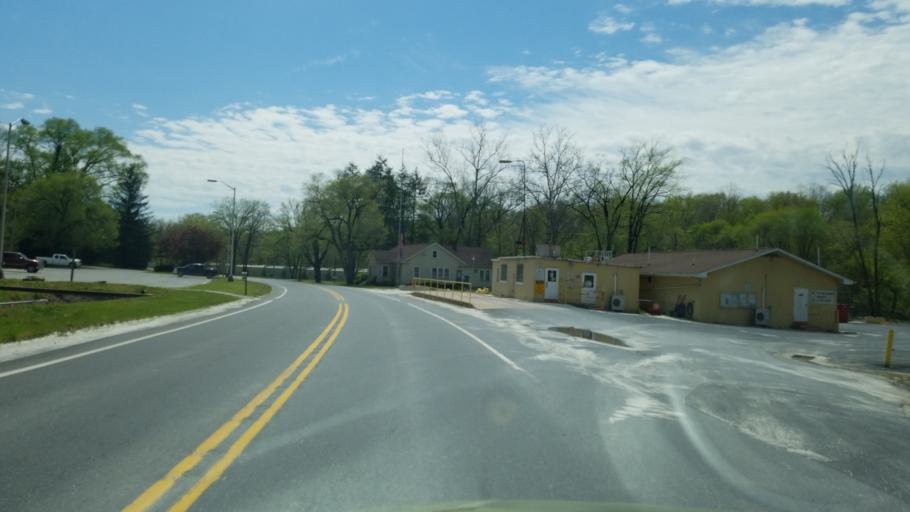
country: US
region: Pennsylvania
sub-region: Huntingdon County
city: Mount Union
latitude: 40.4075
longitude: -77.9365
